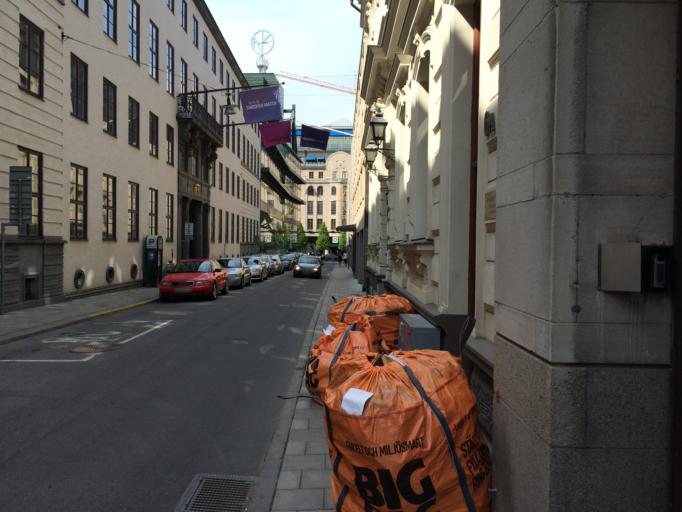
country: SE
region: Stockholm
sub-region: Stockholms Kommun
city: Stockholm
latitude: 59.3315
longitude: 18.0699
